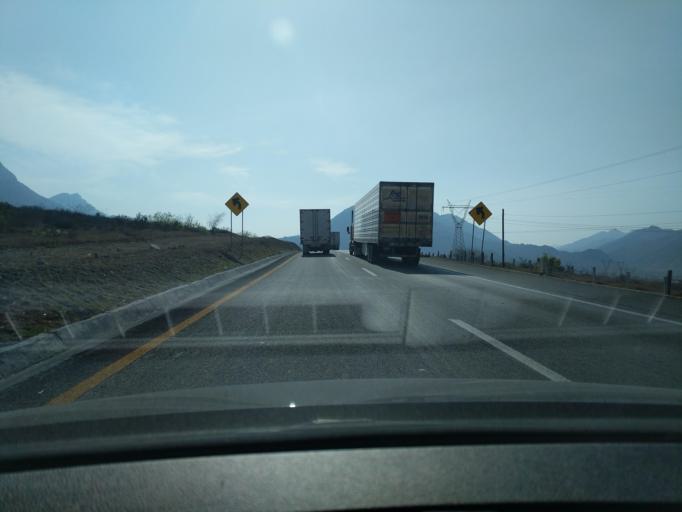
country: MX
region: Nuevo Leon
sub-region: Garcia
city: Las Torres de Guadalupe
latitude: 25.6731
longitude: -100.6901
